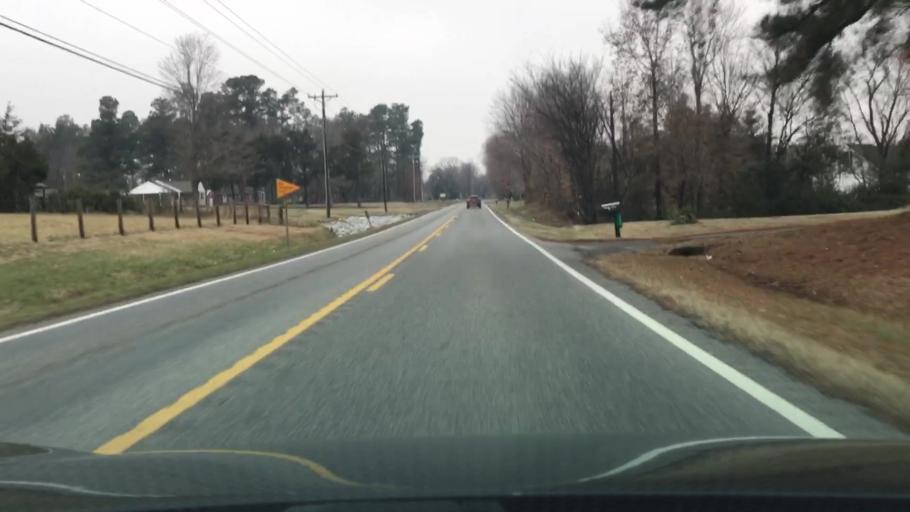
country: US
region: Kentucky
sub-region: Livingston County
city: Ledbetter
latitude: 36.9675
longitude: -88.4534
